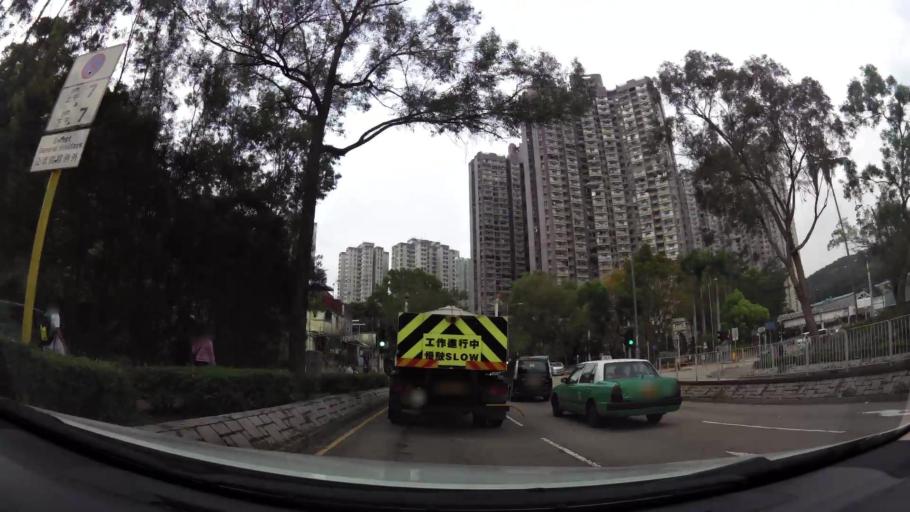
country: HK
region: Tai Po
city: Tai Po
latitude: 22.4427
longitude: 114.1661
